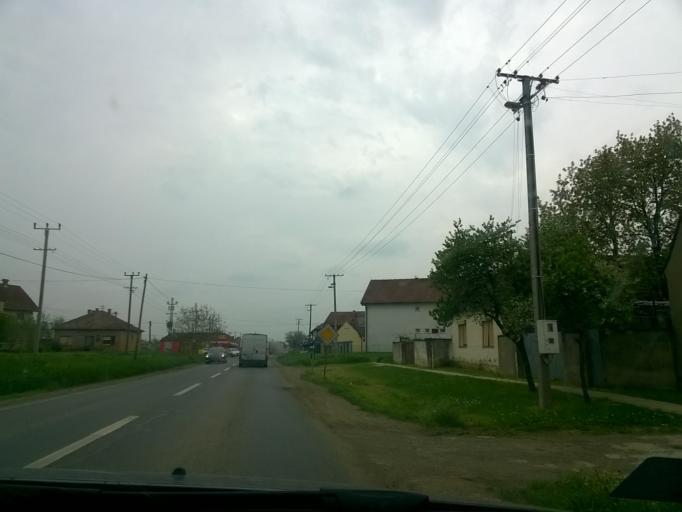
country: RS
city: Platicevo
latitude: 44.8277
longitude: 19.7785
